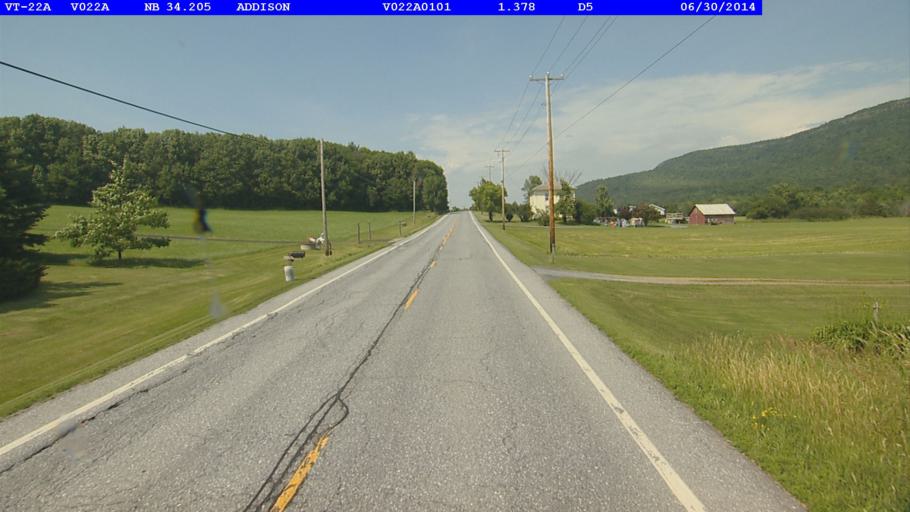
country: US
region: Vermont
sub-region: Addison County
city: Vergennes
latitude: 44.0495
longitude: -73.3024
